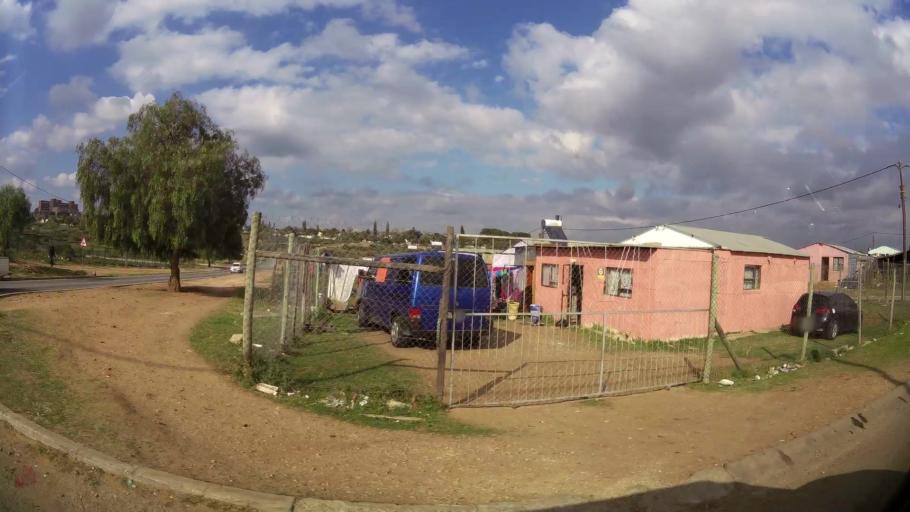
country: ZA
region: Eastern Cape
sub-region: Nelson Mandela Bay Metropolitan Municipality
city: Uitenhage
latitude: -33.7445
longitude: 25.3971
